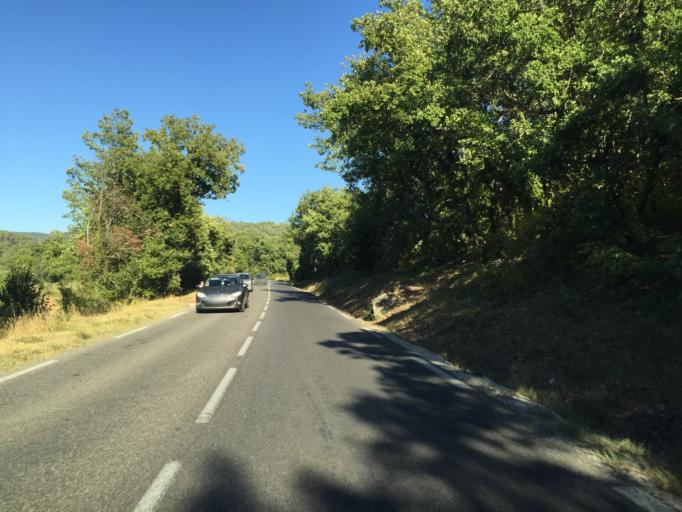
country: FR
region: Provence-Alpes-Cote d'Azur
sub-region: Departement du Vaucluse
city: Saignon
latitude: 43.8796
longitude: 5.4347
